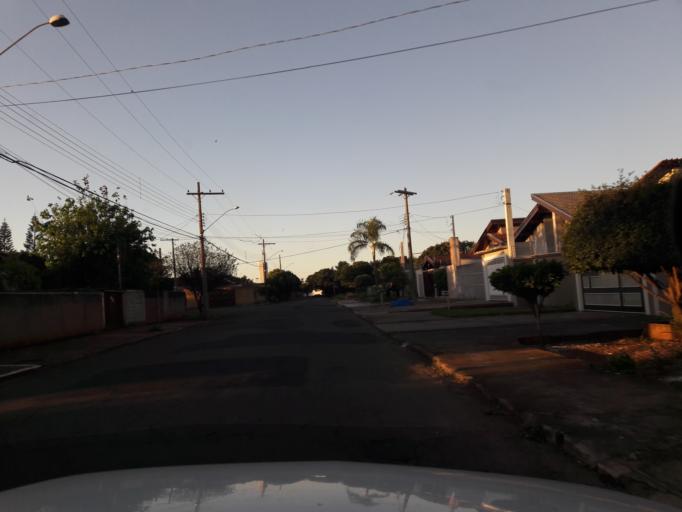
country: BR
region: Sao Paulo
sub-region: Moji-Guacu
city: Mogi-Gaucu
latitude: -22.3500
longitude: -46.9344
